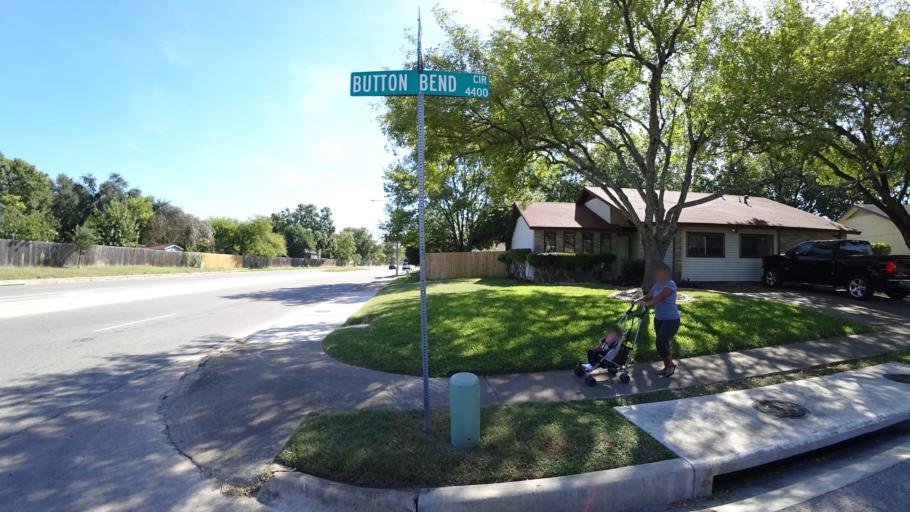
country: US
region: Texas
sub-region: Travis County
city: Austin
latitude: 30.2016
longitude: -97.7423
